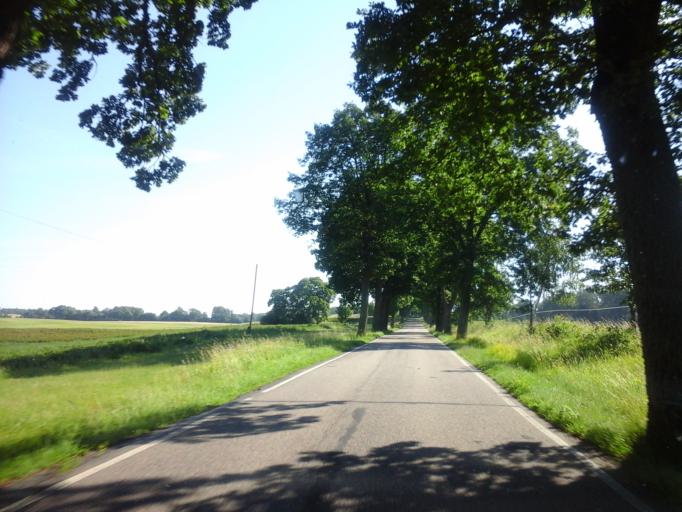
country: PL
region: West Pomeranian Voivodeship
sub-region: Powiat drawski
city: Drawsko Pomorskie
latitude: 53.5786
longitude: 15.8792
